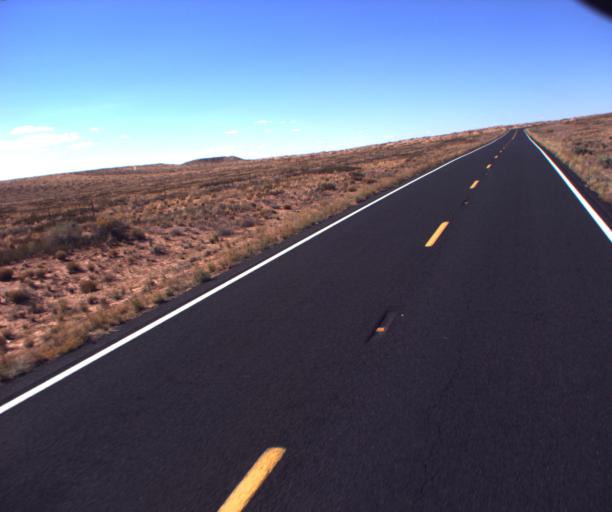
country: US
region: Arizona
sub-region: Coconino County
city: Tuba City
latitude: 36.0350
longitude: -111.1799
